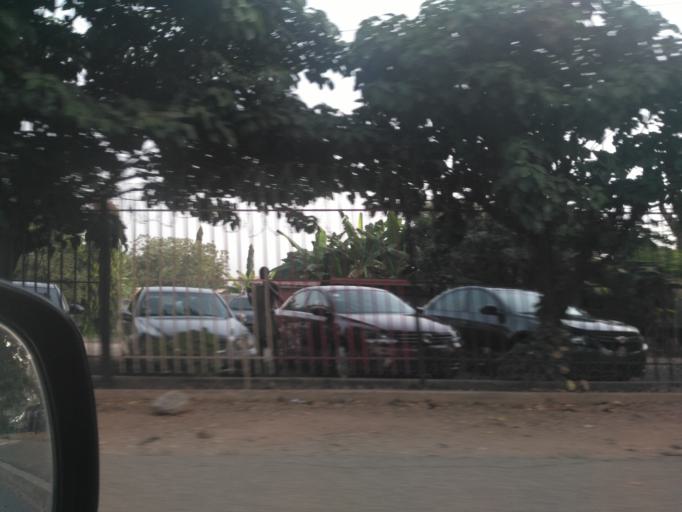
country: GH
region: Greater Accra
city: Accra
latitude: 5.6036
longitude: -0.2014
